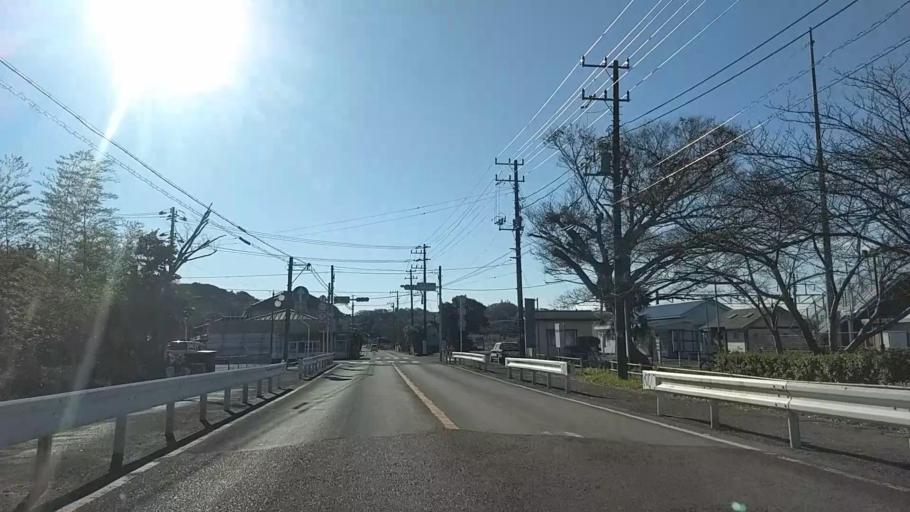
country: JP
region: Chiba
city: Kimitsu
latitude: 35.2614
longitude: 139.8762
